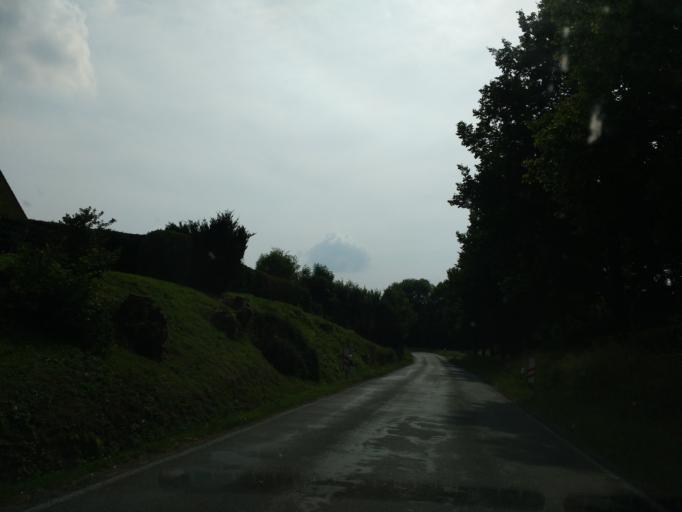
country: DE
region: North Rhine-Westphalia
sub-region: Regierungsbezirk Detmold
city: Horn
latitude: 51.8737
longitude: 8.9576
